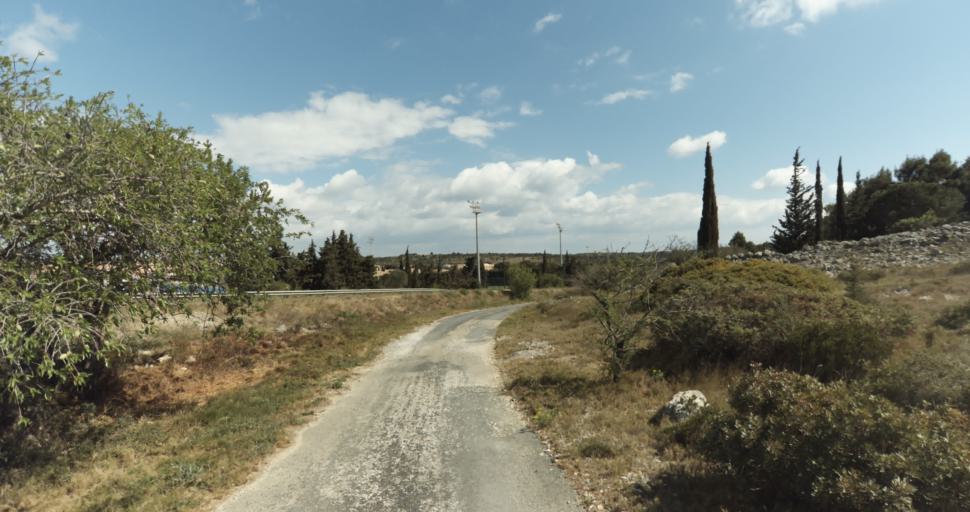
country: FR
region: Languedoc-Roussillon
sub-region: Departement de l'Aude
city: Leucate
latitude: 42.9021
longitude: 3.0317
